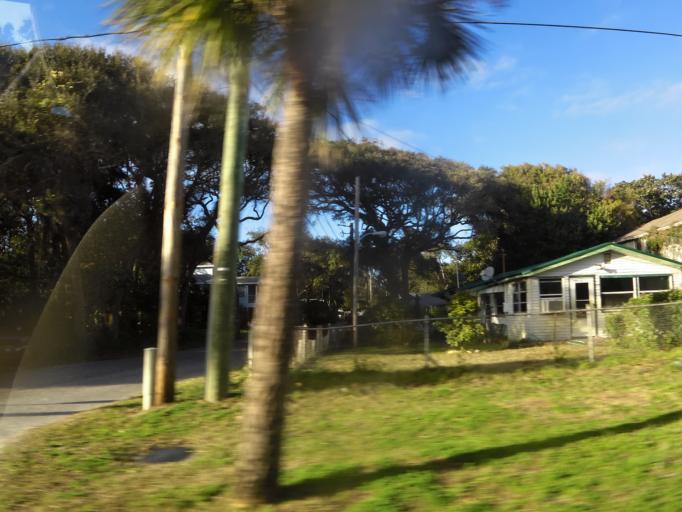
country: US
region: Florida
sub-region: Nassau County
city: Fernandina Beach
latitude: 30.5736
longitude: -81.4467
